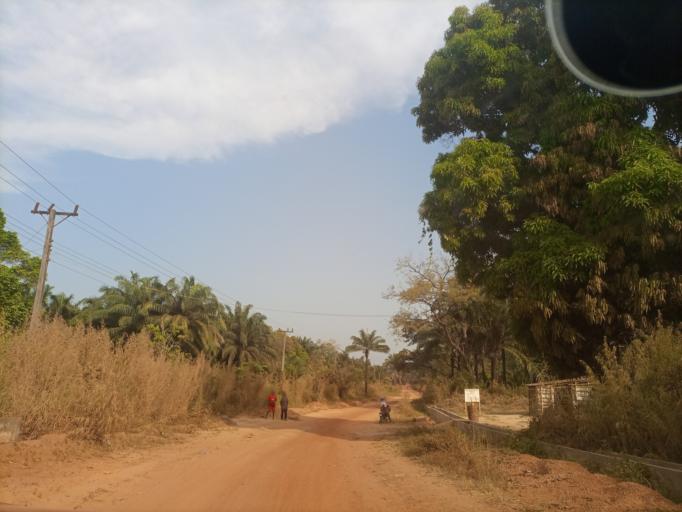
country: NG
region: Enugu
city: Obolo-Eke (1)
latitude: 6.8091
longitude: 7.5538
